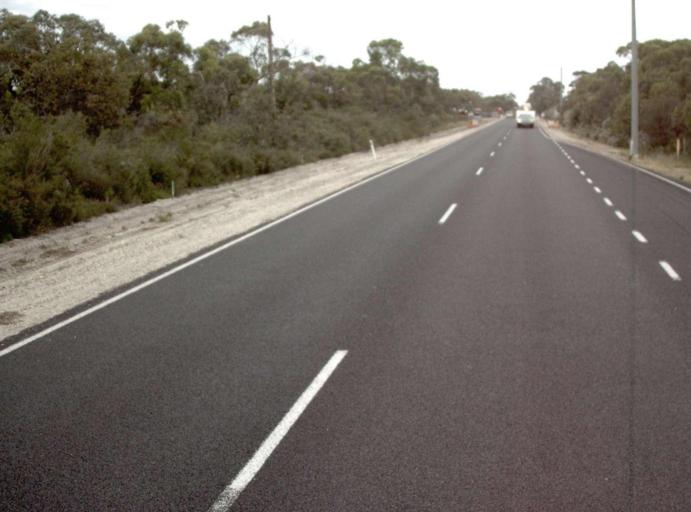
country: AU
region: Victoria
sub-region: East Gippsland
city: Bairnsdale
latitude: -38.1261
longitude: 147.4321
